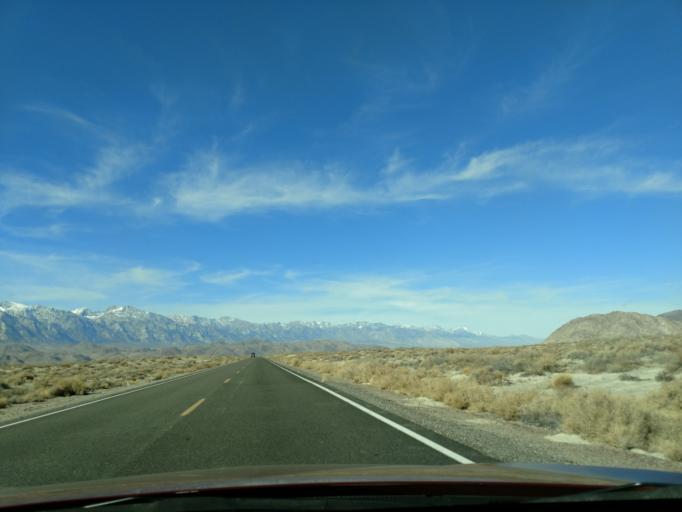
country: US
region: California
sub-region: Inyo County
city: Lone Pine
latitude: 36.5604
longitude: -117.9687
